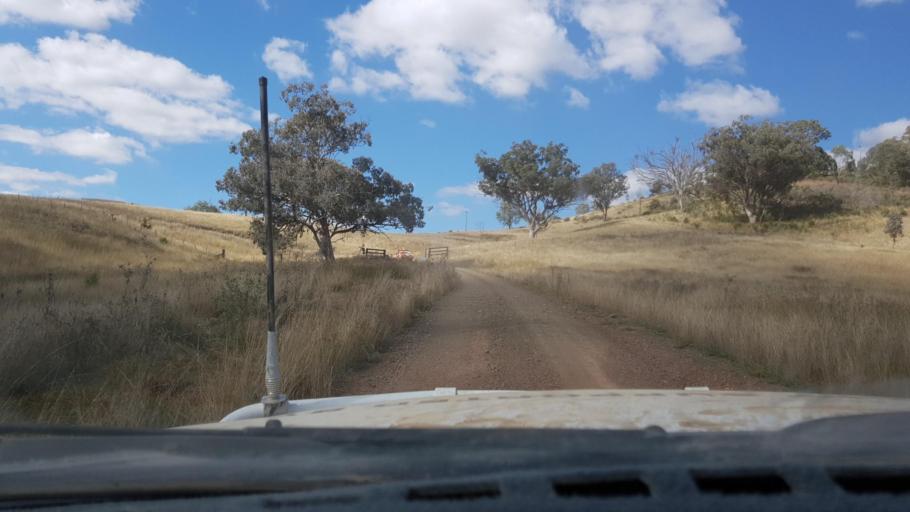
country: AU
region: New South Wales
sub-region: Tamworth Municipality
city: Manilla
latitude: -30.4331
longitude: 150.8013
